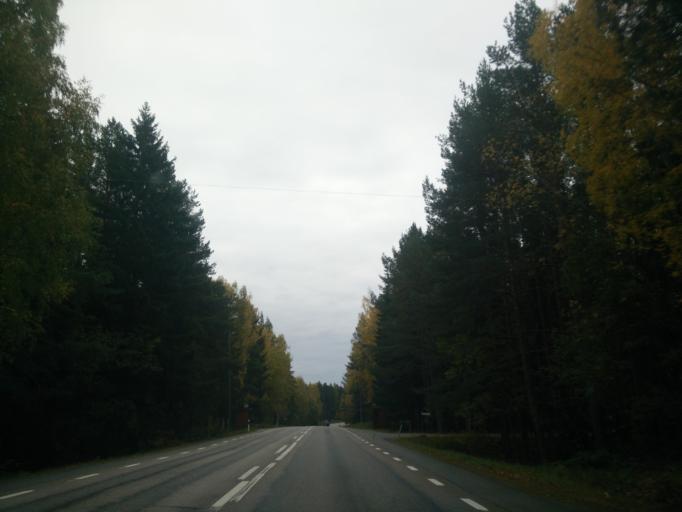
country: SE
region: Gaevleborg
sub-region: Gavle Kommun
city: Norrsundet
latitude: 60.8897
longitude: 17.1201
